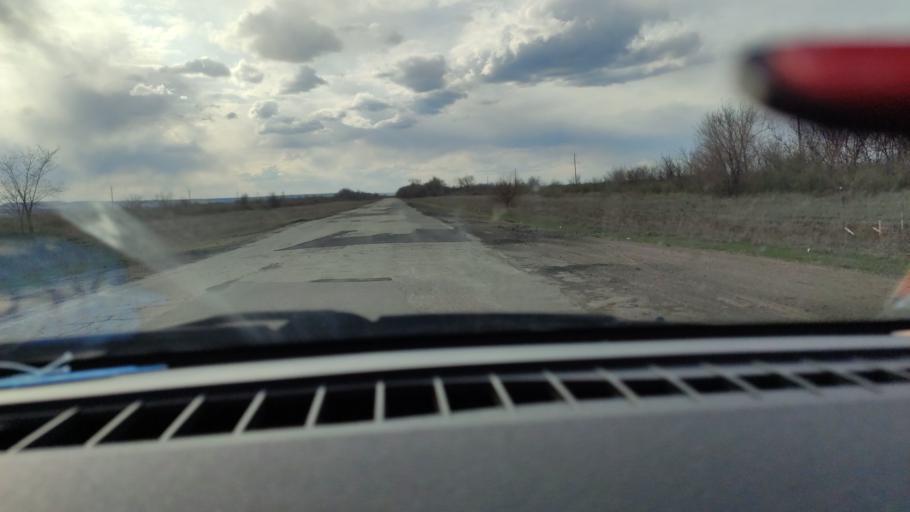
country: RU
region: Saratov
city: Rovnoye
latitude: 51.0673
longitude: 46.0014
